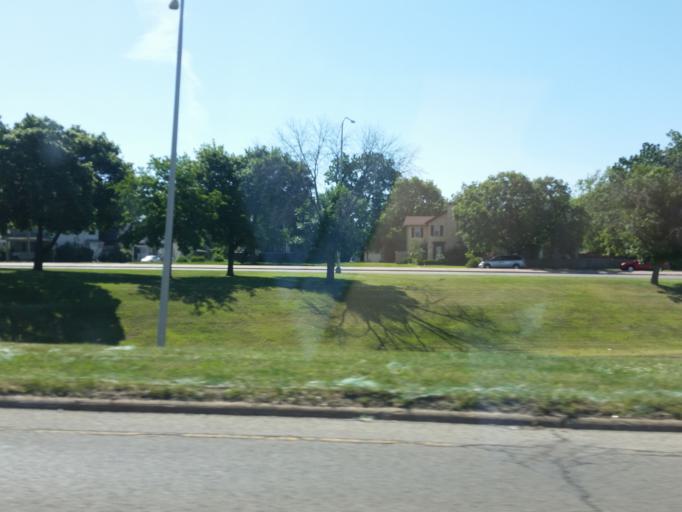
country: US
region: Illinois
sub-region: Winnebago County
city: Rockford
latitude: 42.2733
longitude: -89.0816
